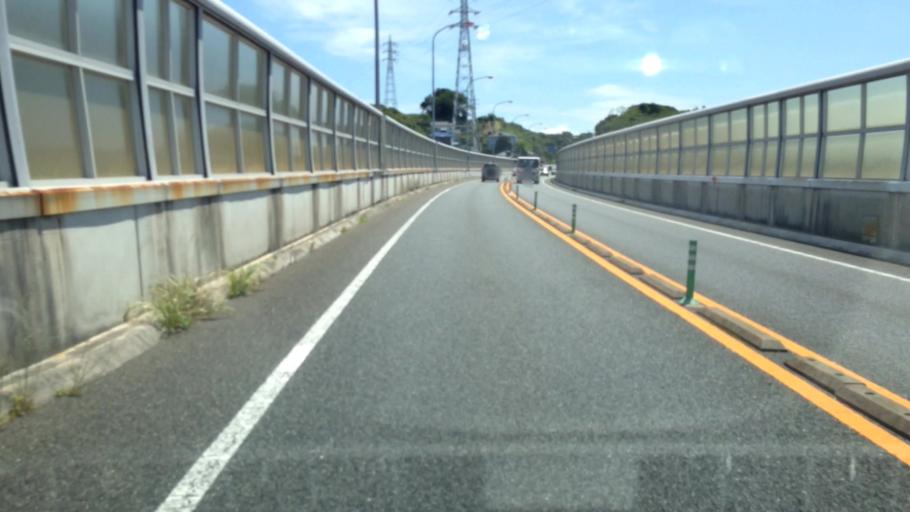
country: JP
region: Kanagawa
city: Yokosuka
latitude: 35.2182
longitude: 139.6374
